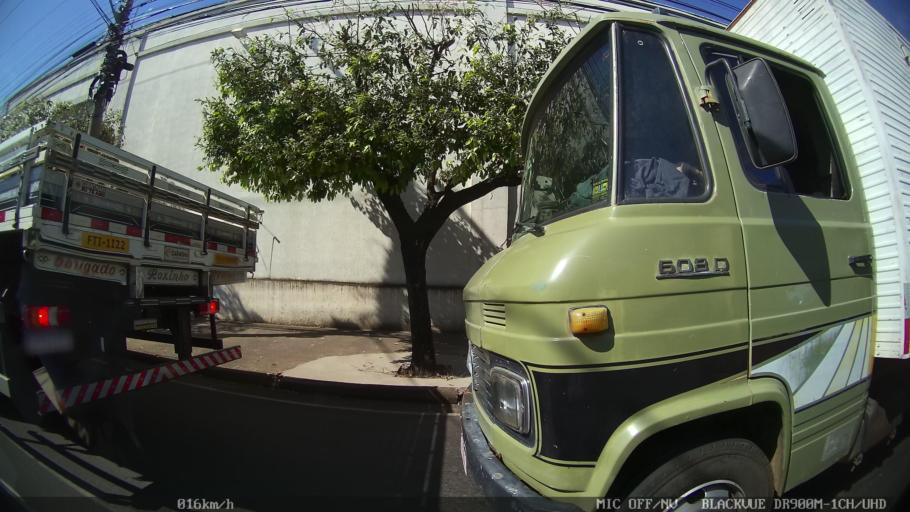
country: BR
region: Sao Paulo
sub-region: Sao Jose Do Rio Preto
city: Sao Jose do Rio Preto
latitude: -20.8001
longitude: -49.3958
